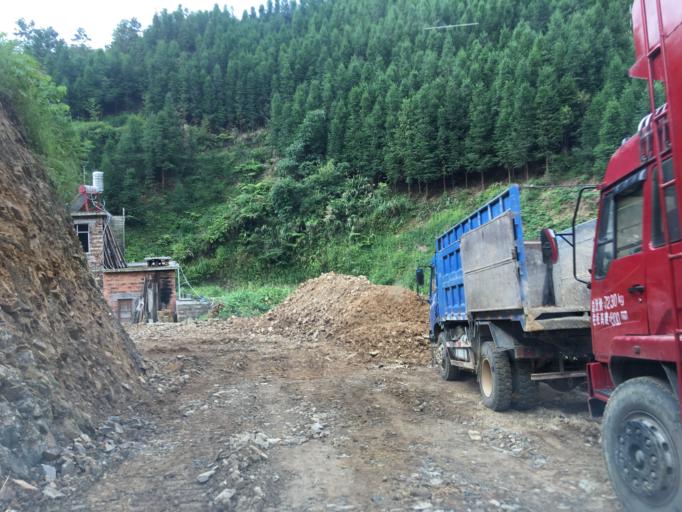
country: CN
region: Guangxi Zhuangzu Zizhiqu
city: Xinzhou
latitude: 24.8681
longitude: 105.8666
